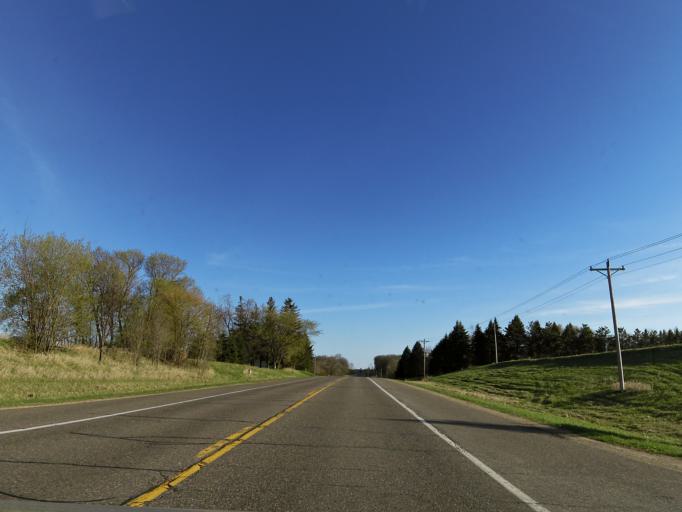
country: US
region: Minnesota
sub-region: Dakota County
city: Lakeville
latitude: 44.5727
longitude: -93.2077
